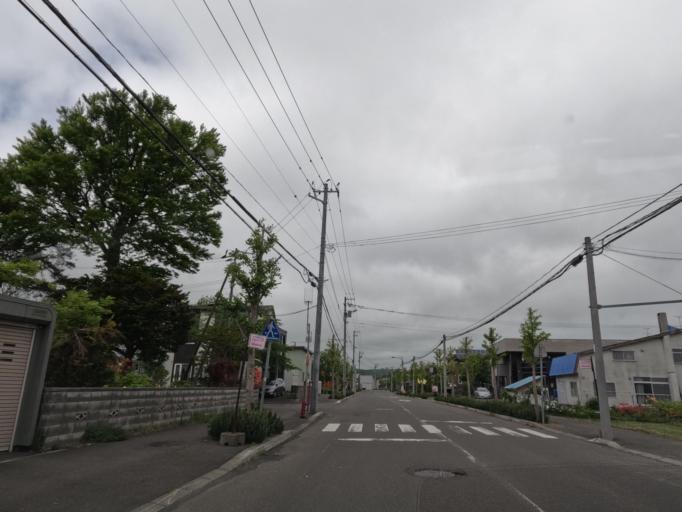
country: JP
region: Hokkaido
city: Tobetsu
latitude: 43.2308
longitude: 141.5163
